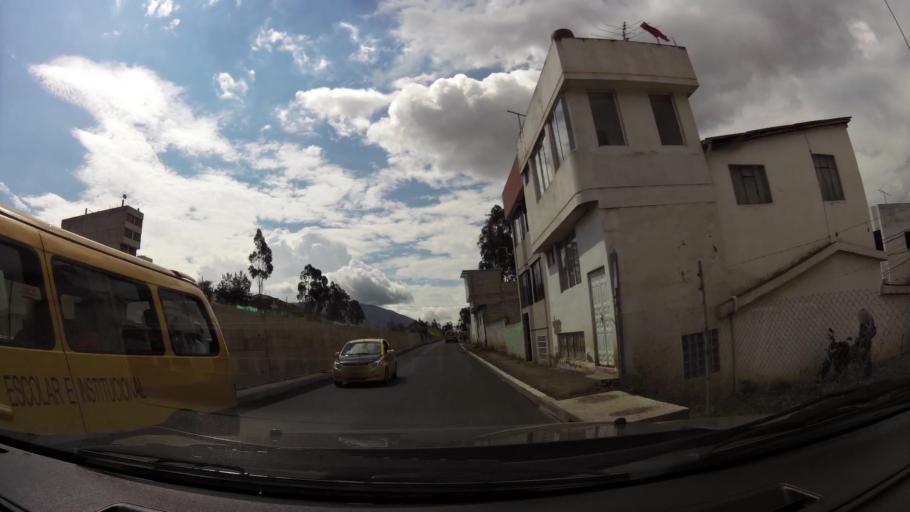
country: EC
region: Pichincha
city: Quito
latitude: -0.1040
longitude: -78.4594
